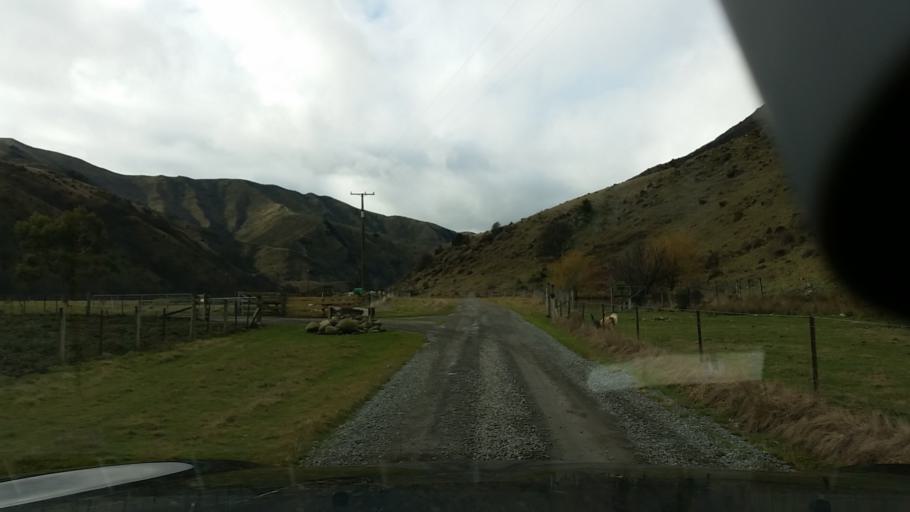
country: NZ
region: Tasman
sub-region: Tasman District
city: Brightwater
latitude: -41.7356
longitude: 173.4254
